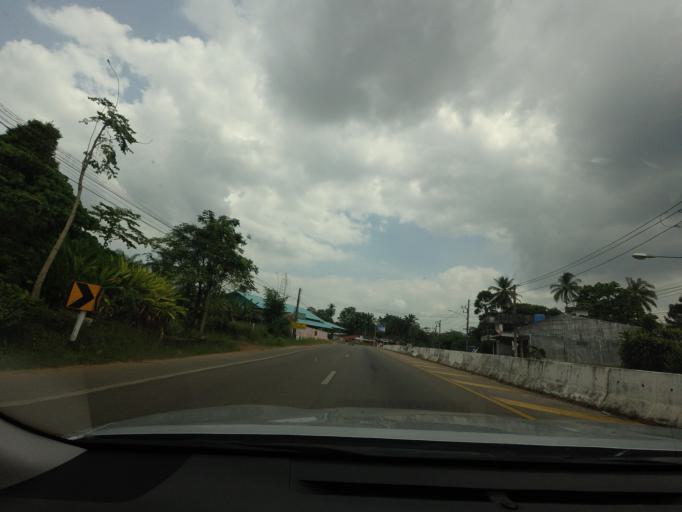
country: TH
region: Phangnga
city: Ban Ao Nang
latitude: 8.0940
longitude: 98.8092
